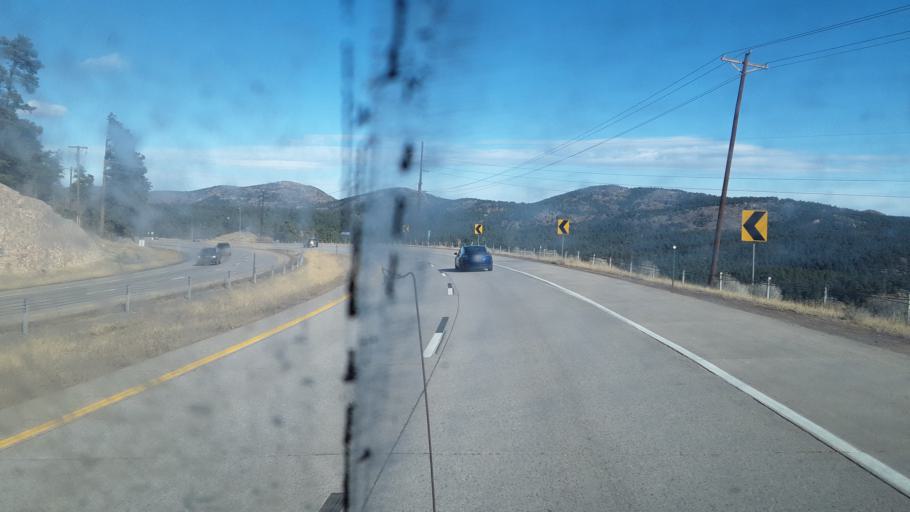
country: US
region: Colorado
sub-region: Jefferson County
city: Indian Hills
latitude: 39.5550
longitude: -105.2410
